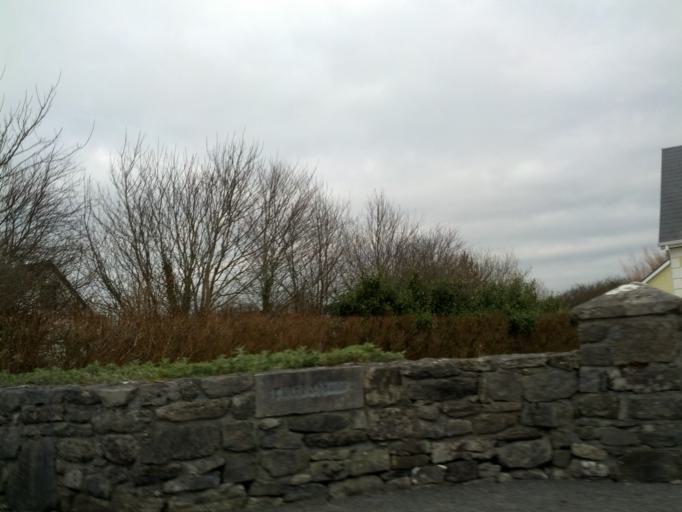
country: IE
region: Connaught
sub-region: County Galway
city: Oranmore
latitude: 53.2027
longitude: -8.9219
